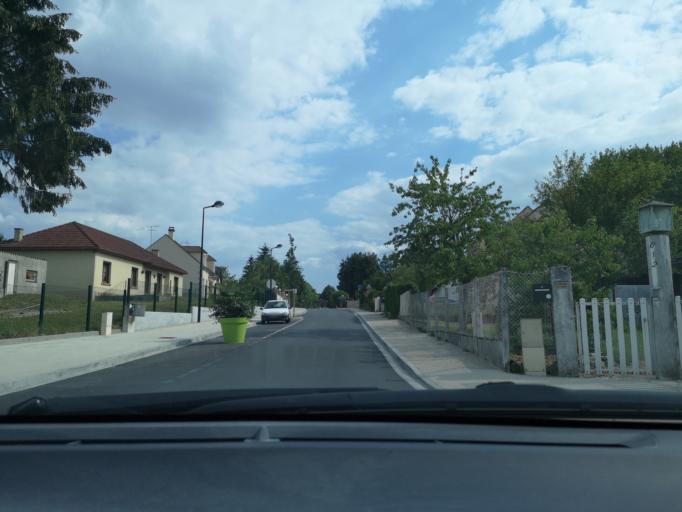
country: FR
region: Centre
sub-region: Departement du Loiret
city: Semoy
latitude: 47.9296
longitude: 1.9589
